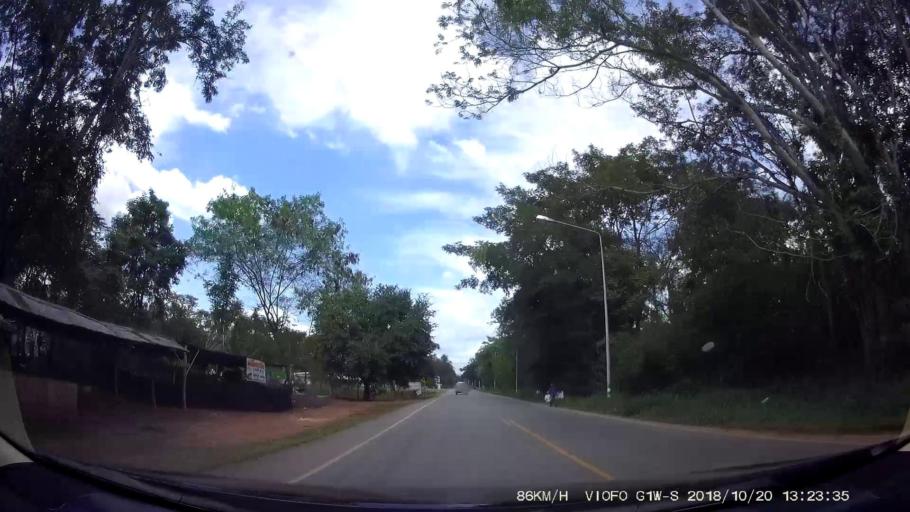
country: TH
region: Chaiyaphum
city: Khon San
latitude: 16.5852
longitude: 101.9223
